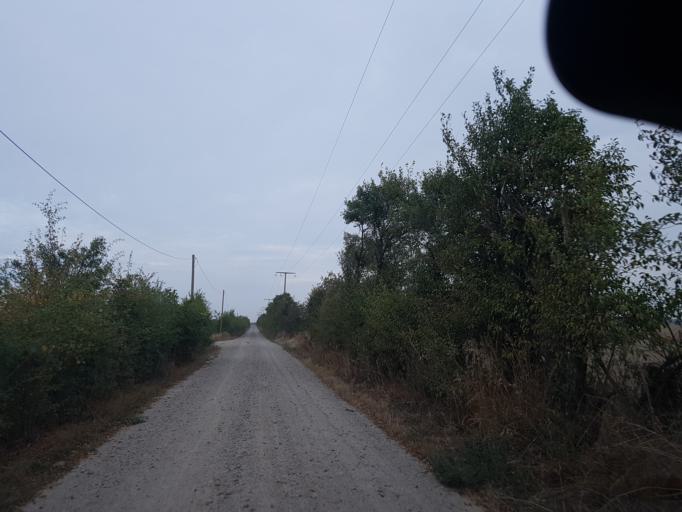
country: DE
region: Saxony-Anhalt
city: Kropstadt
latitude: 52.0036
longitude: 12.8277
